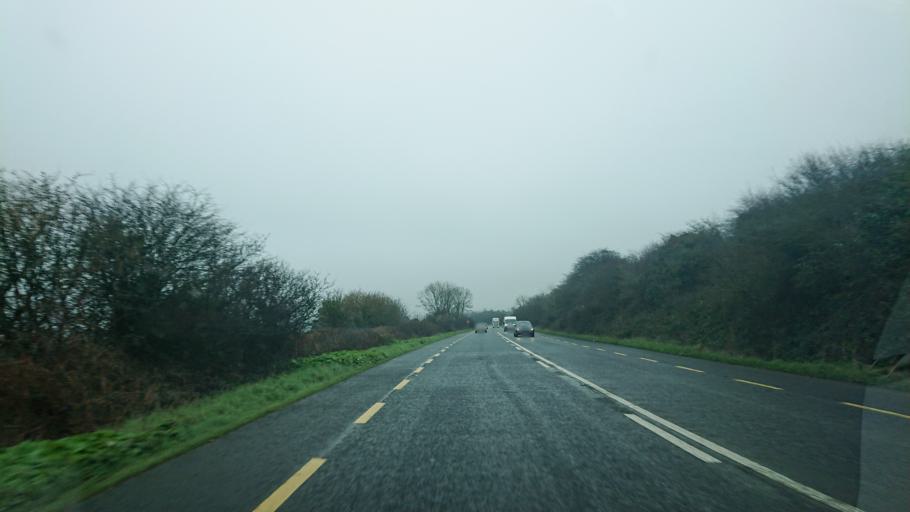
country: IE
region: Munster
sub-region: County Cork
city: Killumney
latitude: 51.7861
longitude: -8.6270
